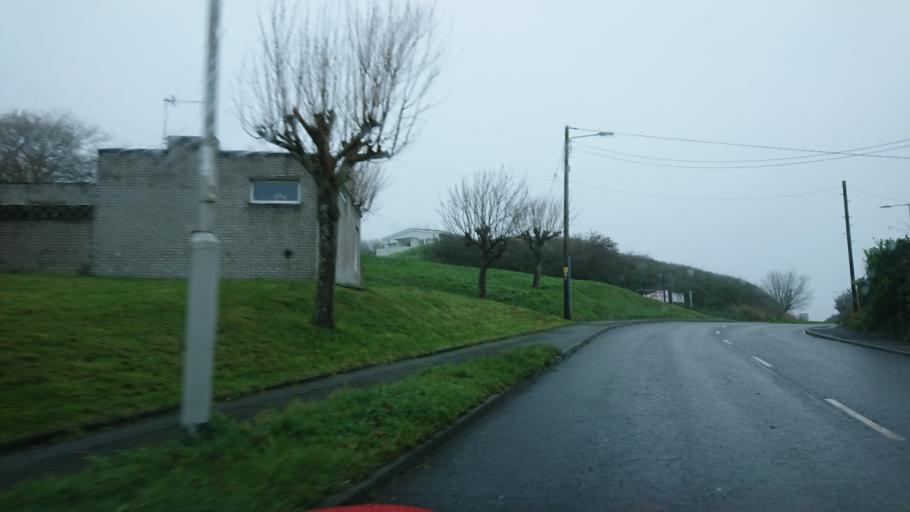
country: GB
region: England
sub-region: Plymouth
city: Plymstock
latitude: 50.3548
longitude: -4.1172
